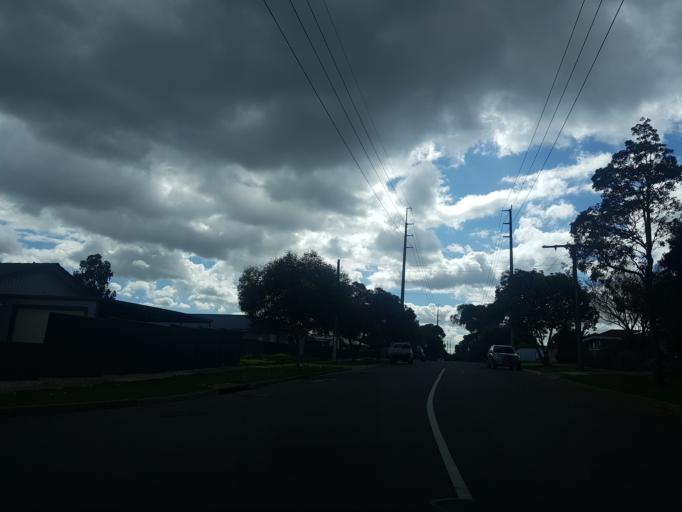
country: AU
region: South Australia
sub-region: Salisbury
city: Ingle Farm
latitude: -34.8252
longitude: 138.6486
